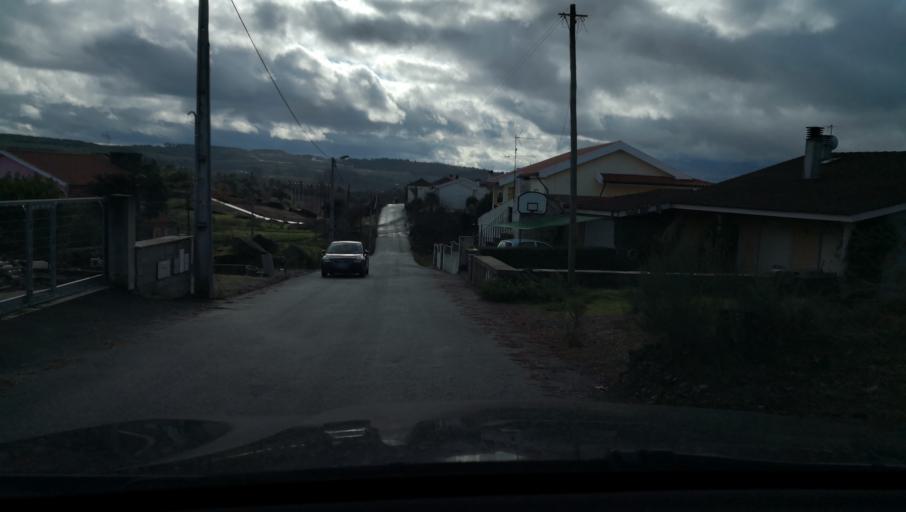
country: PT
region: Vila Real
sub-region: Vila Real
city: Vila Real
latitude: 41.2707
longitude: -7.7259
